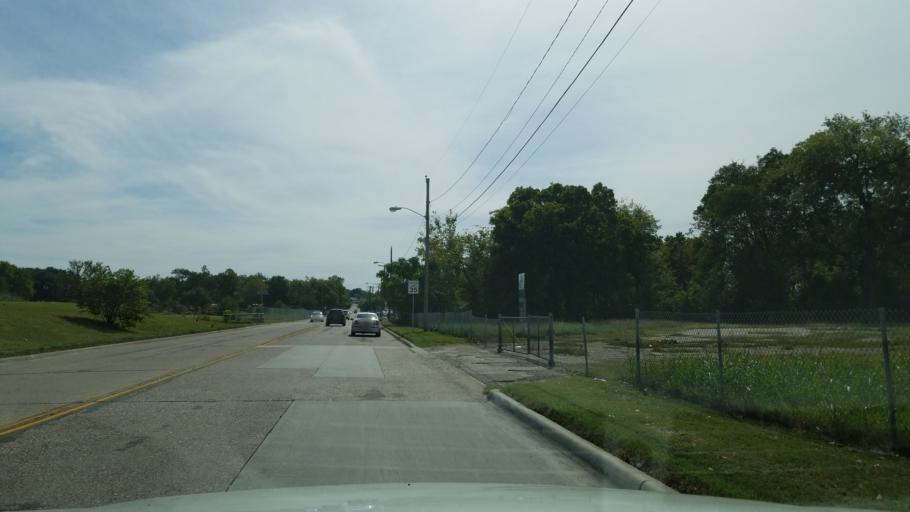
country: US
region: Texas
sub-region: Dallas County
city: Highland Park
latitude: 32.7921
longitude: -96.7261
